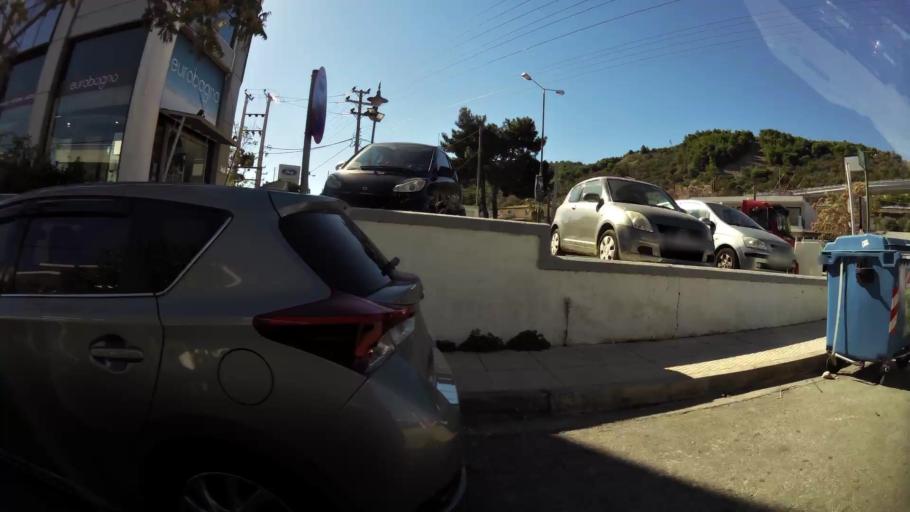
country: GR
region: Attica
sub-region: Nomarchia Athinas
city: Agia Paraskevi
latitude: 38.0084
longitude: 23.8451
